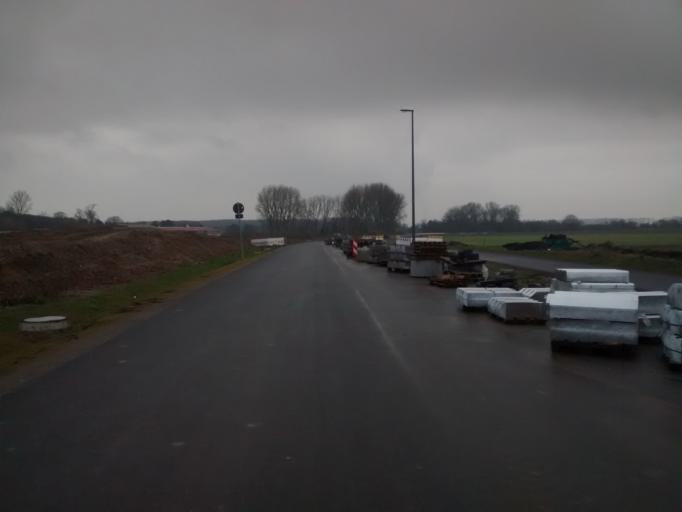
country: DE
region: North Rhine-Westphalia
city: Monheim am Rhein
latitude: 51.0389
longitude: 6.9120
